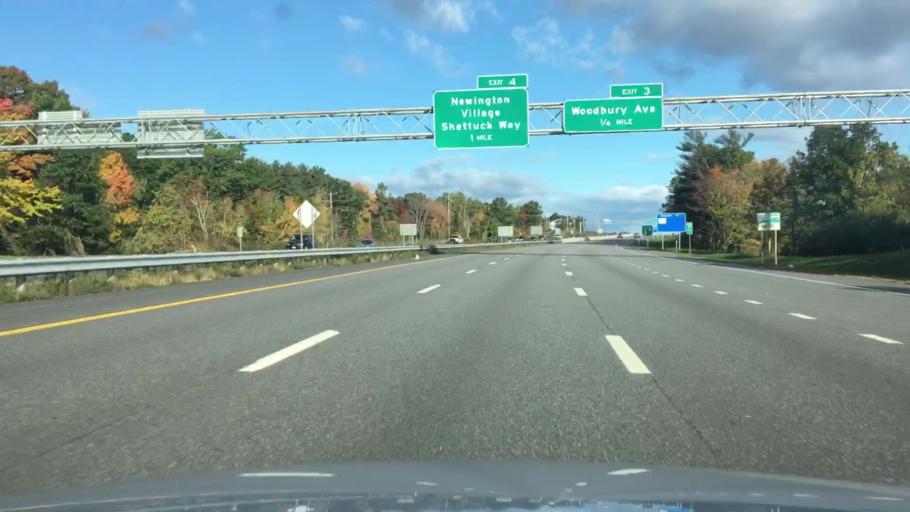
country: US
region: Maine
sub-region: York County
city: South Eliot
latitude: 43.0947
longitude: -70.8070
